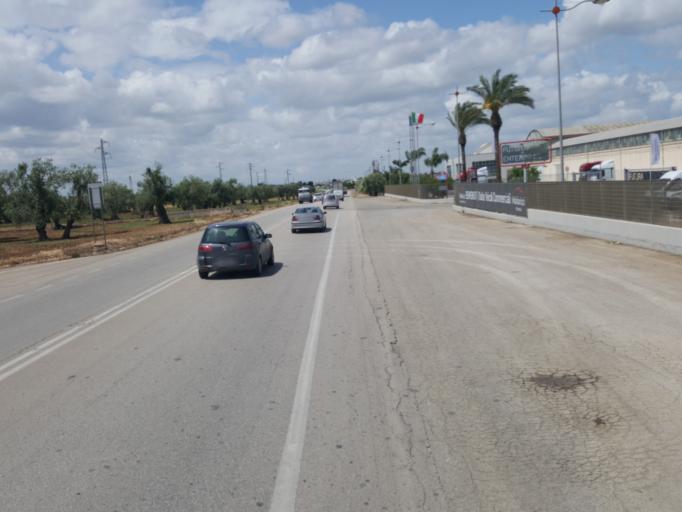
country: IT
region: Apulia
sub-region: Provincia di Bari
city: Modugno
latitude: 41.0943
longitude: 16.7473
